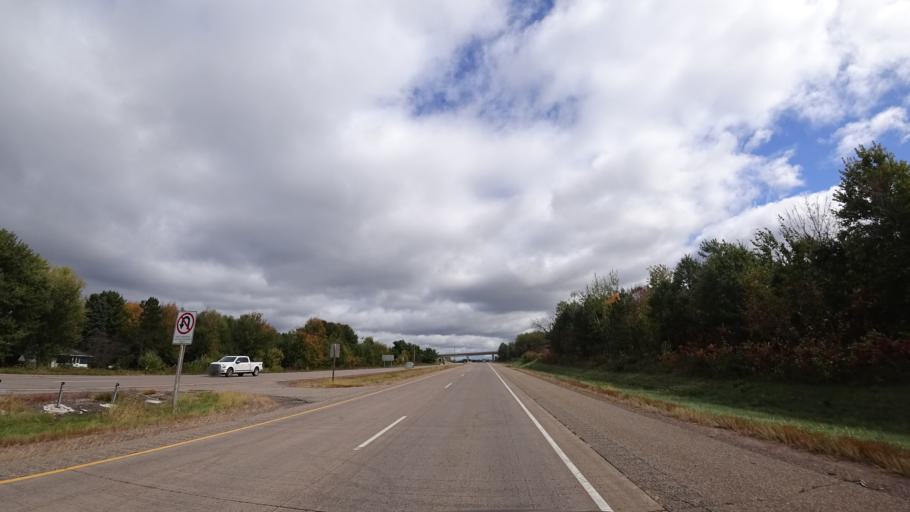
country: US
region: Wisconsin
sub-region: Chippewa County
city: Chippewa Falls
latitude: 44.9198
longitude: -91.3505
